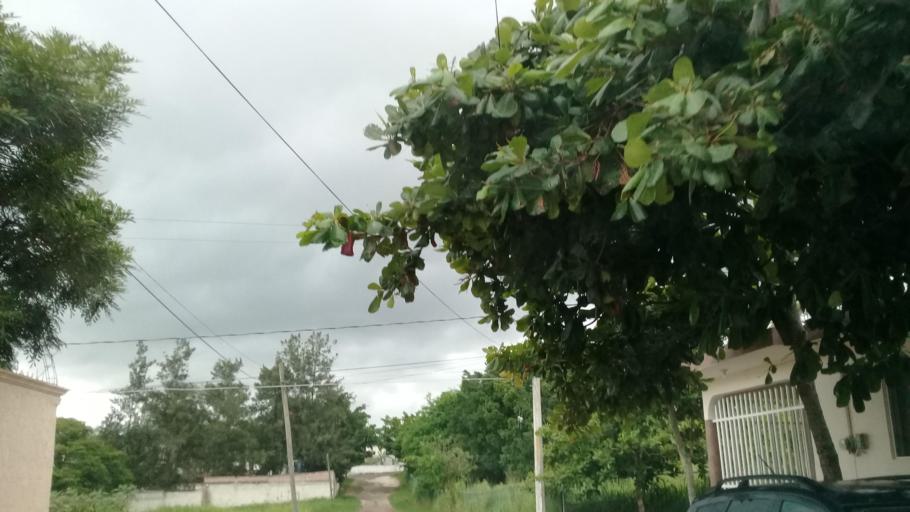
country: MX
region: Veracruz
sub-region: Emiliano Zapata
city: Dos Rios
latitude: 19.4864
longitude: -96.7991
